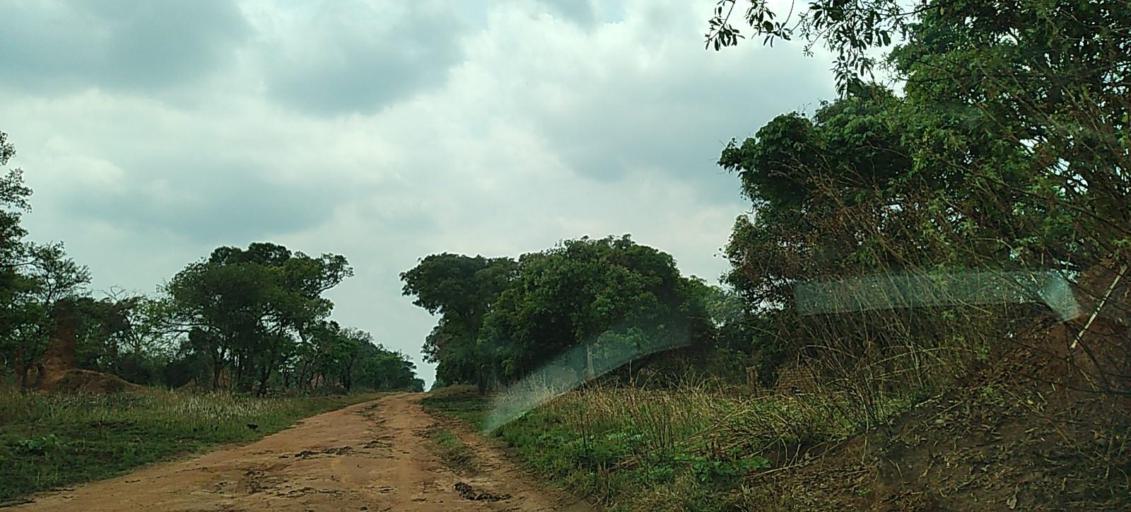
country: ZM
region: North-Western
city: Mwinilunga
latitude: -11.5332
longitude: 24.7842
